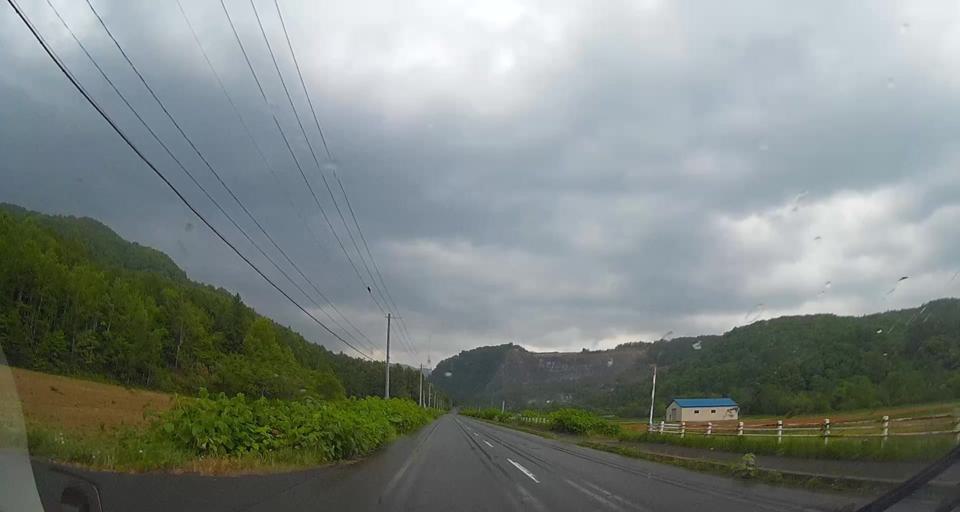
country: JP
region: Hokkaido
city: Niseko Town
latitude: 42.8933
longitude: 140.9000
